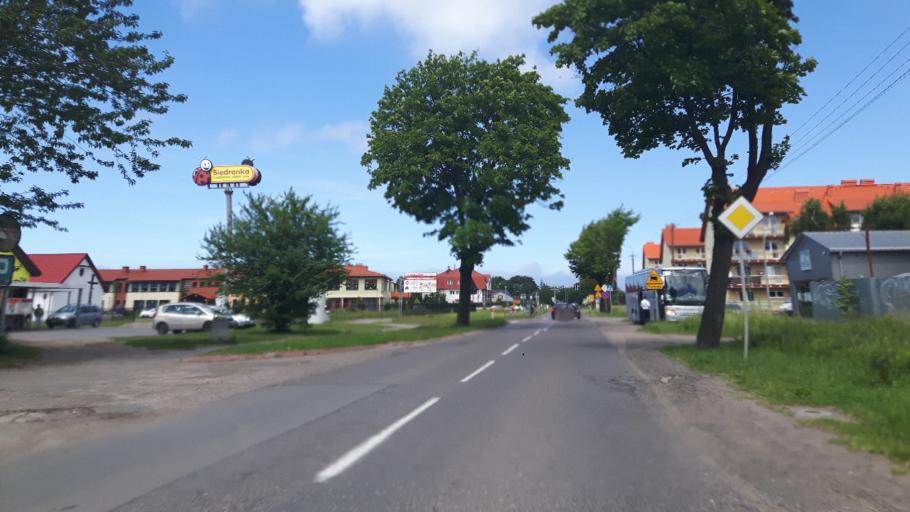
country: PL
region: Pomeranian Voivodeship
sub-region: Powiat slupski
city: Ustka
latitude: 54.5718
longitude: 16.8514
